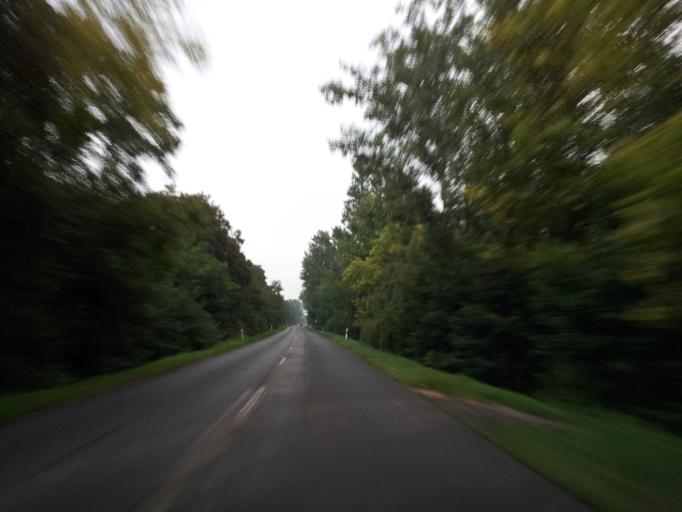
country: HU
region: Tolna
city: Fadd
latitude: 46.4382
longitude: 18.8088
